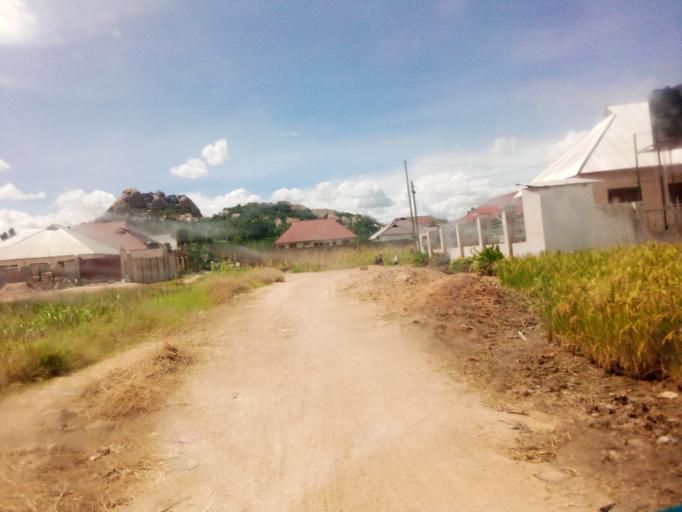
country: TZ
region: Dodoma
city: Dodoma
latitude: -6.1631
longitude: 35.7649
